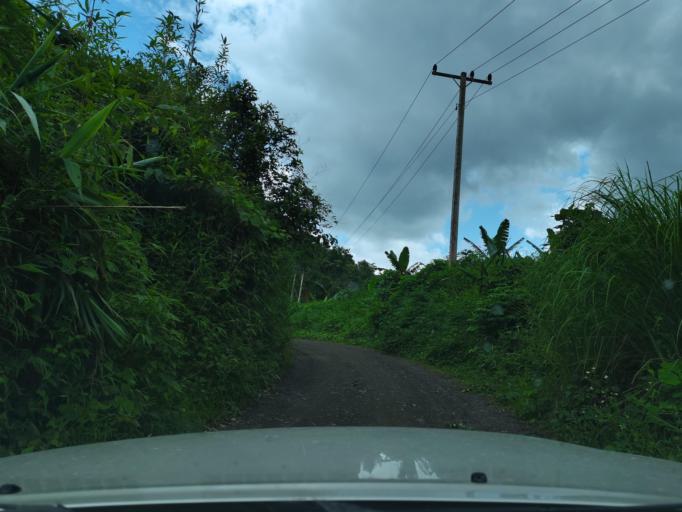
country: LA
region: Loungnamtha
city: Muang Long
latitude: 20.7699
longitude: 101.0174
